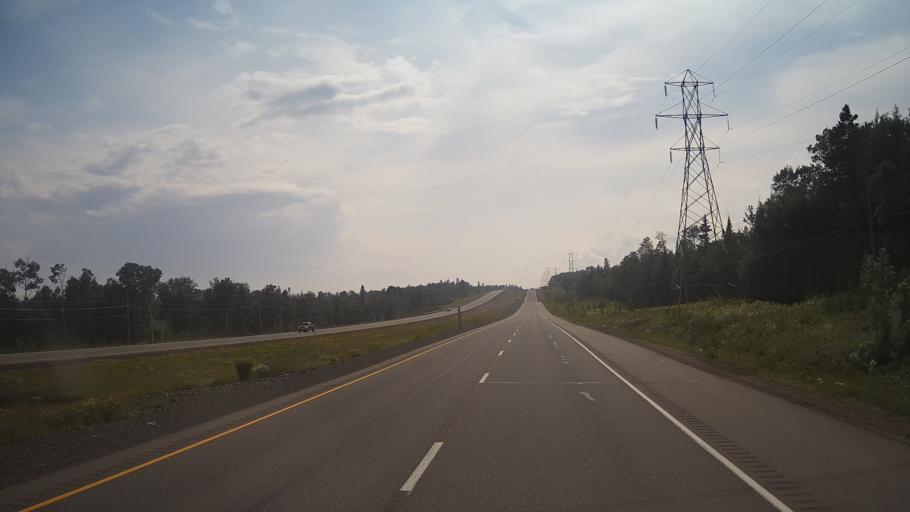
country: CA
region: Ontario
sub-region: Thunder Bay District
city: Thunder Bay
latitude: 48.5768
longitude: -88.8161
